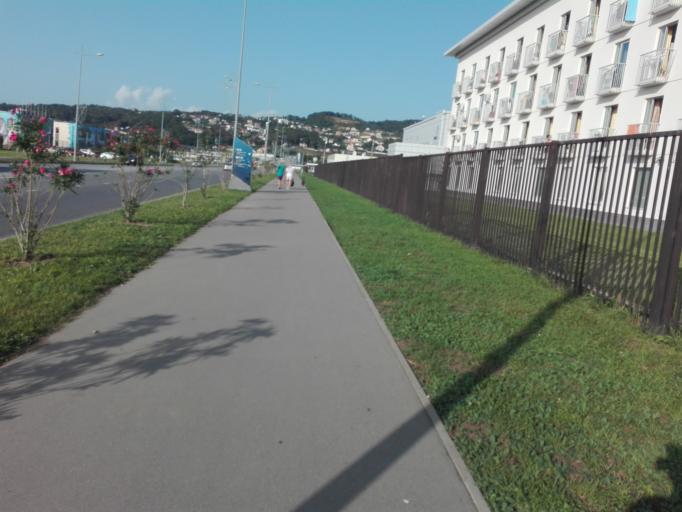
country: RU
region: Krasnodarskiy
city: Adler
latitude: 43.4034
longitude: 39.9707
